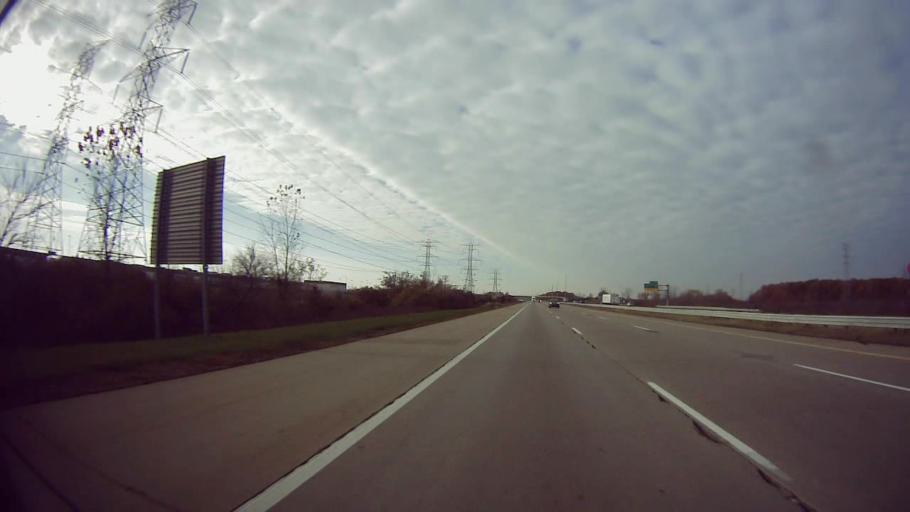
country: US
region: Michigan
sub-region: Monroe County
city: Woodland Beach
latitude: 41.9978
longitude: -83.3214
